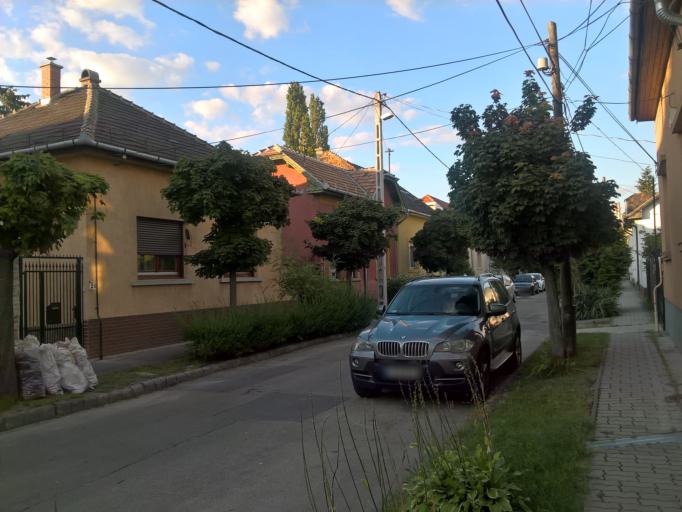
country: HU
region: Budapest
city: Budapest XIX. keruelet
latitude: 47.4523
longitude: 19.1597
